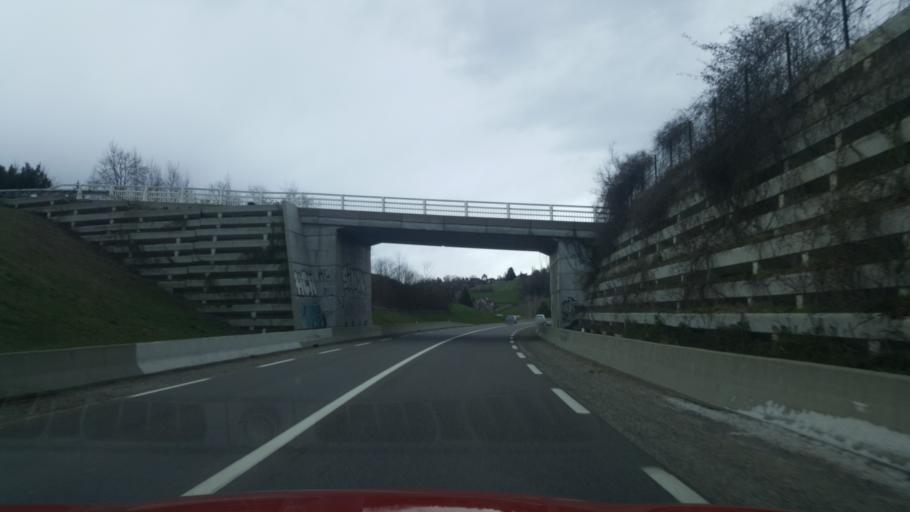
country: FR
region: Rhone-Alpes
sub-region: Departement de la Haute-Savoie
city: La Balme-de-Sillingy
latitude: 45.9605
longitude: 6.0350
